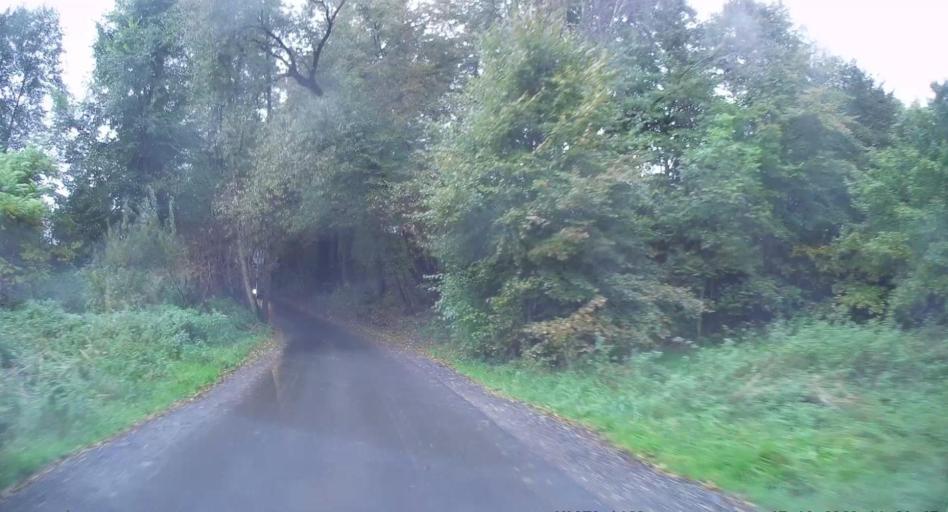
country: PL
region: Lesser Poland Voivodeship
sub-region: Powiat krakowski
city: Ochojno
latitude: 49.9888
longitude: 19.9887
